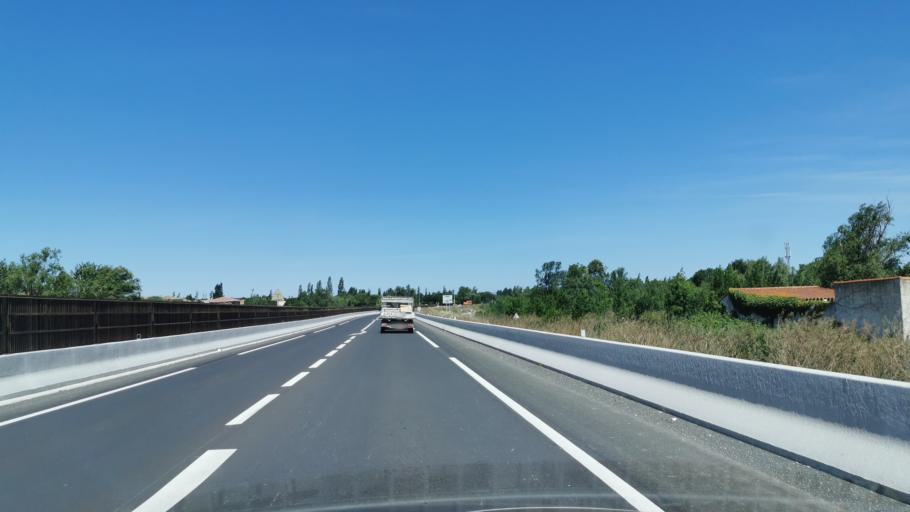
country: FR
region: Languedoc-Roussillon
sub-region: Departement de l'Aude
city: Narbonne
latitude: 43.1983
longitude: 3.0238
